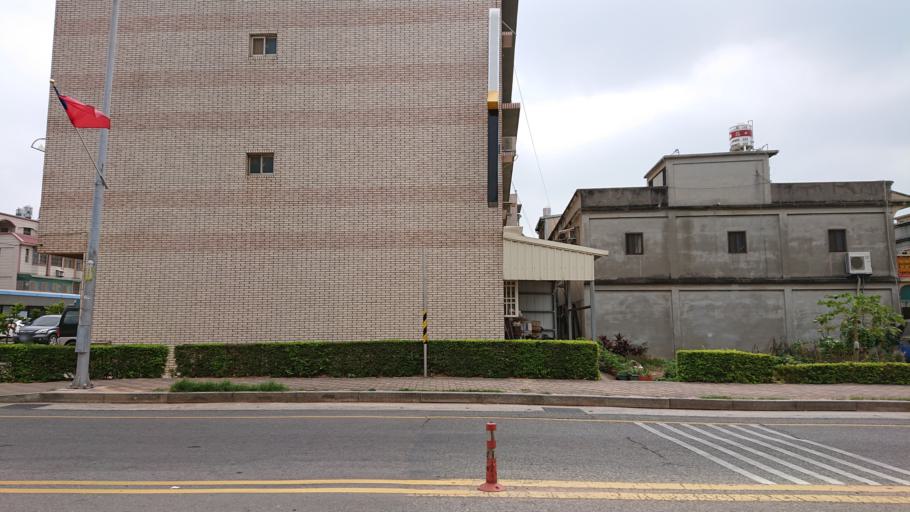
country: TW
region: Fukien
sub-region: Kinmen
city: Jincheng
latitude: 24.4392
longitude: 118.3203
